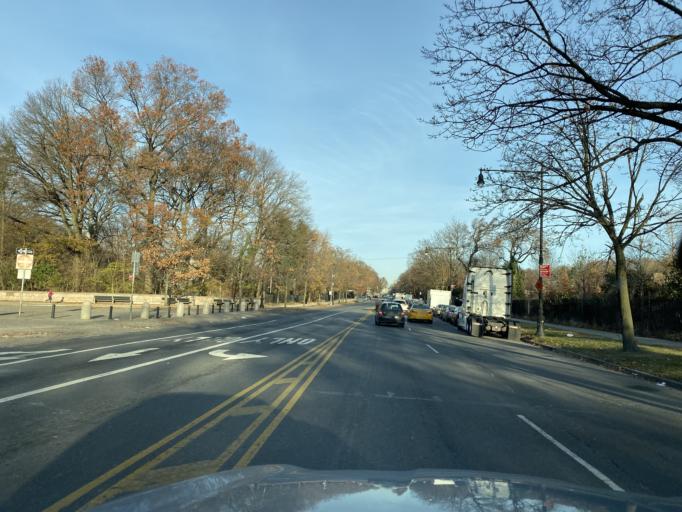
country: US
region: New York
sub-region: Kings County
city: Brooklyn
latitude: 40.6636
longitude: -73.9627
